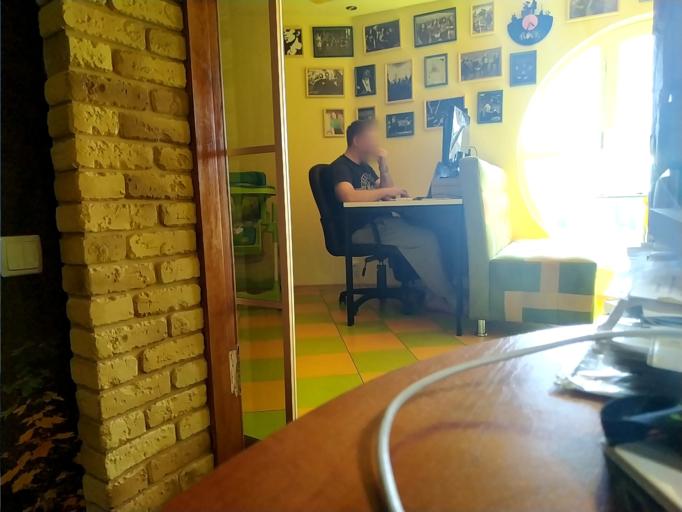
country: RU
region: Moskovskaya
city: Rakhmanovo
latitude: 55.7384
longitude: 38.5917
